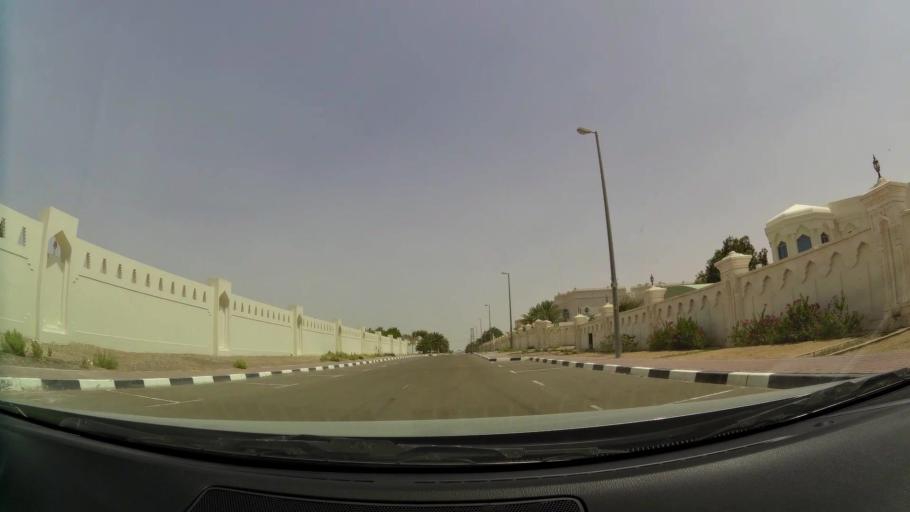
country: AE
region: Abu Dhabi
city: Al Ain
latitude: 24.1892
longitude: 55.6796
